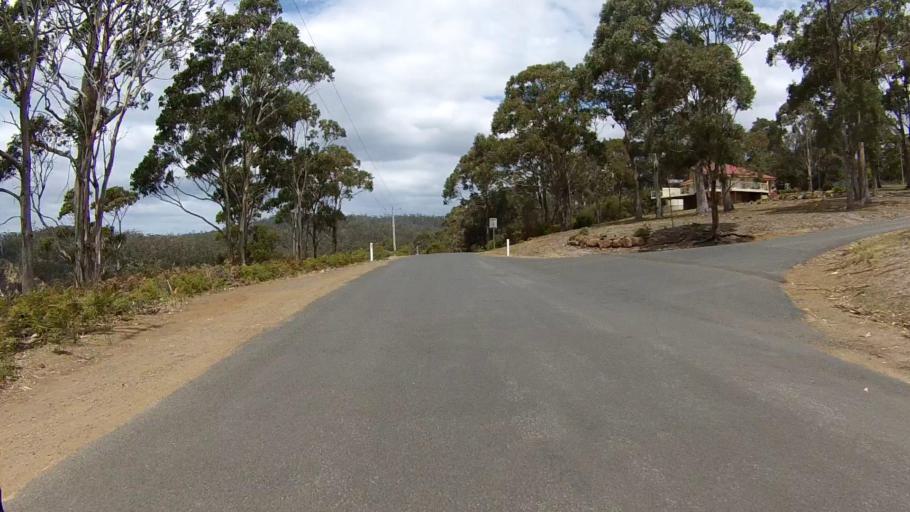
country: AU
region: Tasmania
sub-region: Sorell
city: Sorell
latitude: -42.5872
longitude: 147.9147
